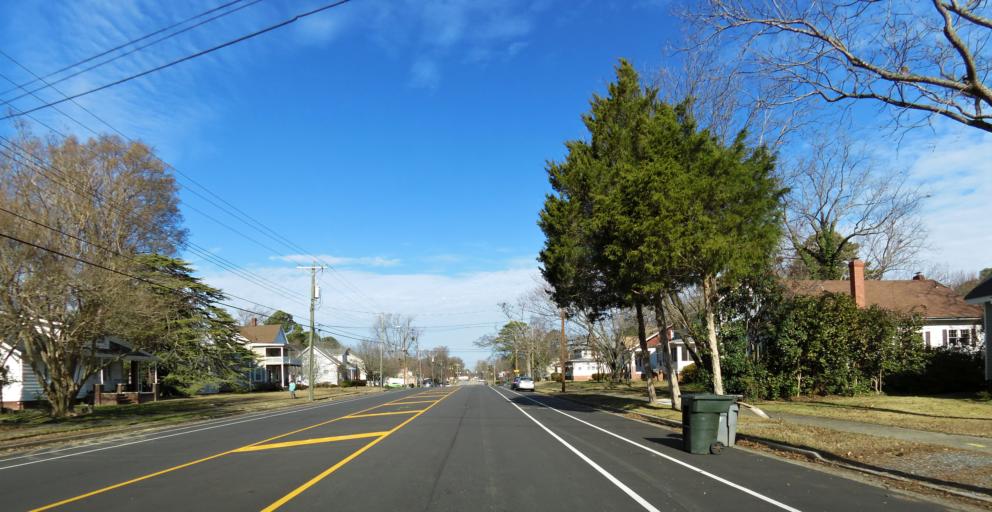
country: US
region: Virginia
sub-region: City of Hampton
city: Hampton
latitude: 37.0051
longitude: -76.3593
